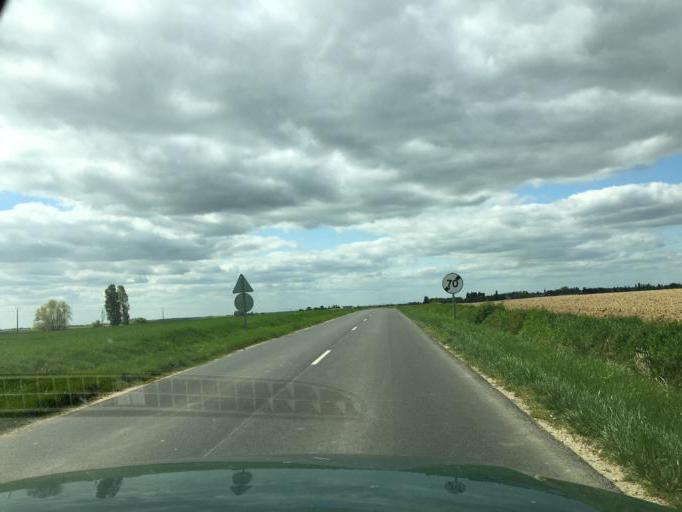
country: FR
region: Centre
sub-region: Departement du Loir-et-Cher
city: Oucques
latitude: 47.8150
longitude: 1.4235
